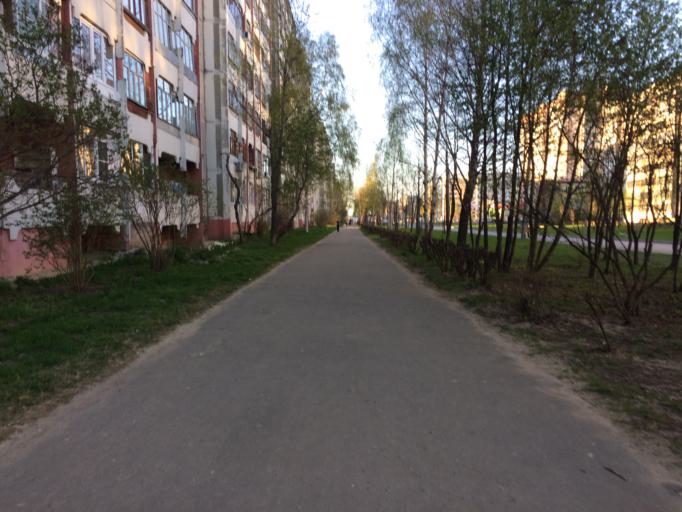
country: RU
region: Mariy-El
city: Yoshkar-Ola
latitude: 56.6280
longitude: 47.9155
